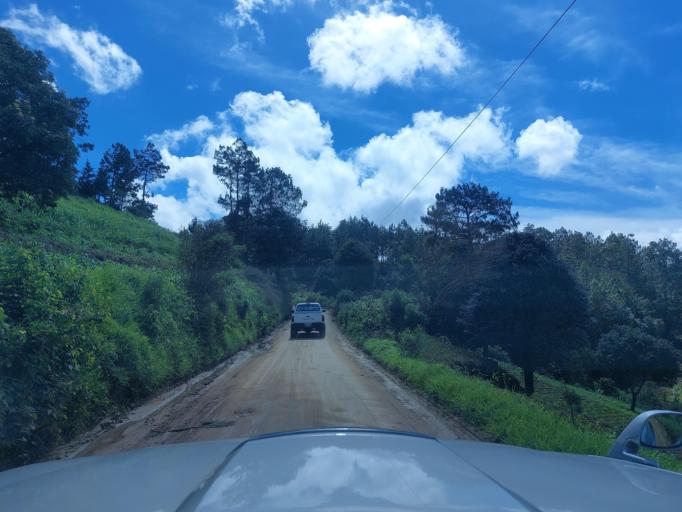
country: GT
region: Chimaltenango
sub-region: Municipio de San Juan Comalapa
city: Comalapa
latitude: 14.7568
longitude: -90.8880
